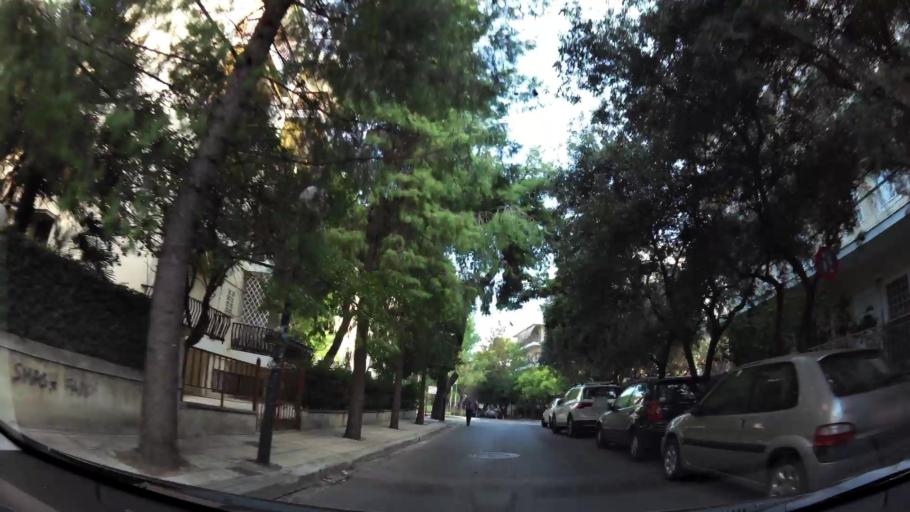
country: GR
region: Attica
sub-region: Nomarchia Athinas
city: Irakleio
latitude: 38.0440
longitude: 23.7678
